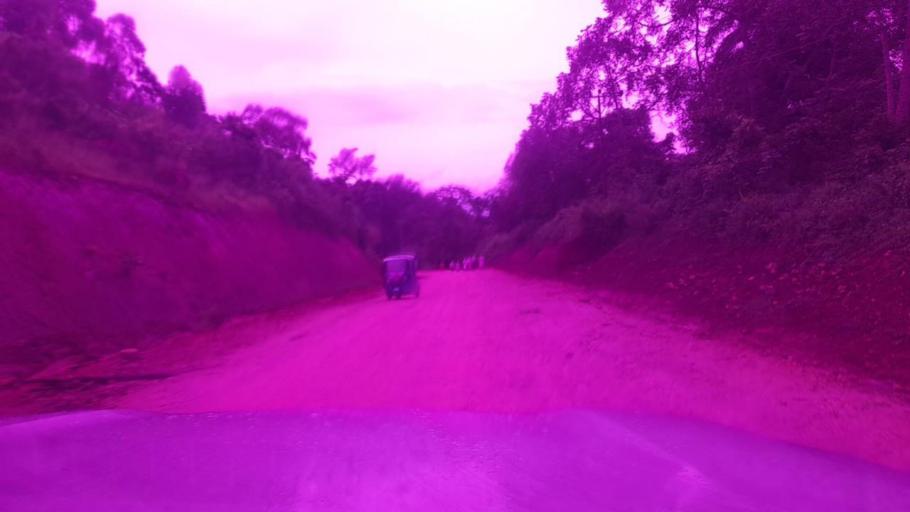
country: ET
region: Southern Nations, Nationalities, and People's Region
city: Bonga
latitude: 7.4462
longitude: 36.1458
